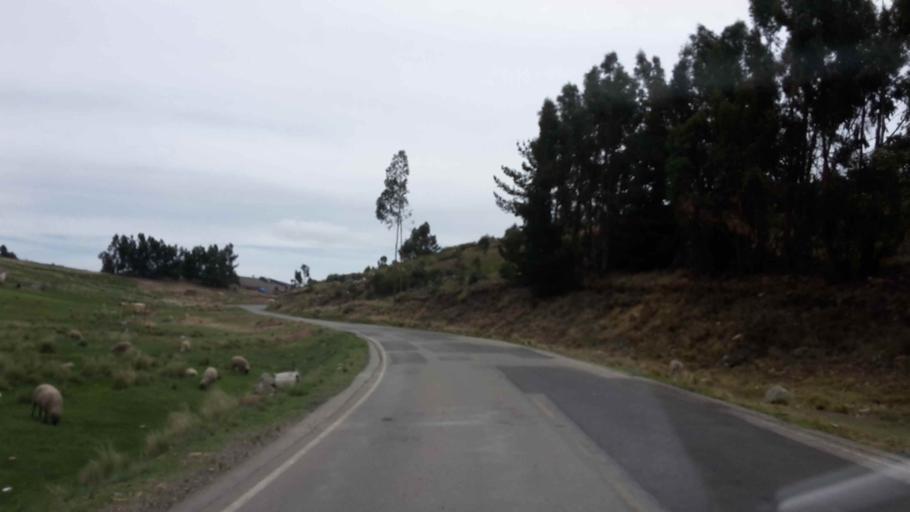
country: BO
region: Cochabamba
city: Arani
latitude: -17.4847
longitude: -65.6064
